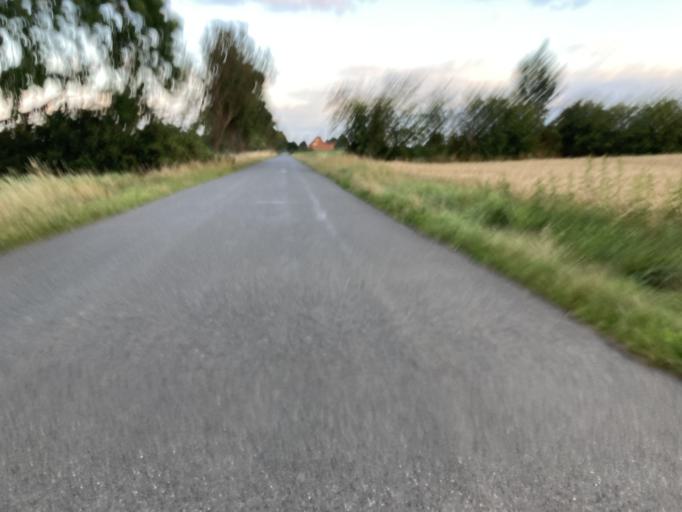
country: DE
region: Lower Saxony
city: Verden
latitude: 52.9266
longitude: 9.2006
